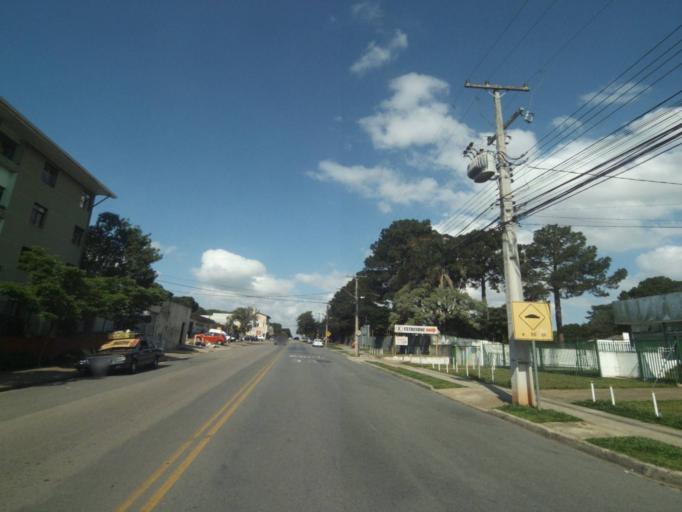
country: BR
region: Parana
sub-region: Curitiba
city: Curitiba
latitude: -25.4959
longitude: -49.3175
